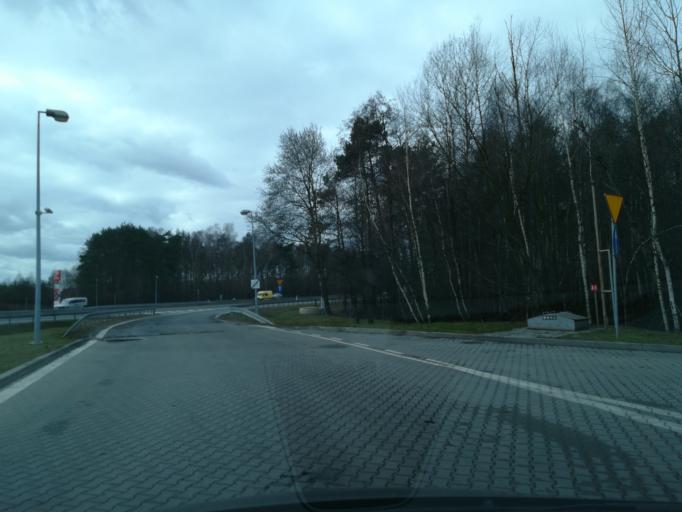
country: PL
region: Lesser Poland Voivodeship
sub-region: Powiat chrzanowski
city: Libiaz
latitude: 50.1491
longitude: 19.2972
